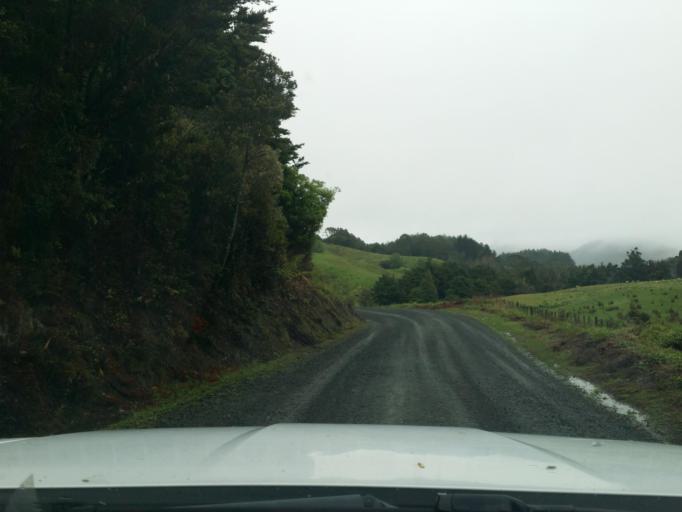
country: NZ
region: Northland
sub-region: Kaipara District
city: Dargaville
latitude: -35.7558
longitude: 173.9244
